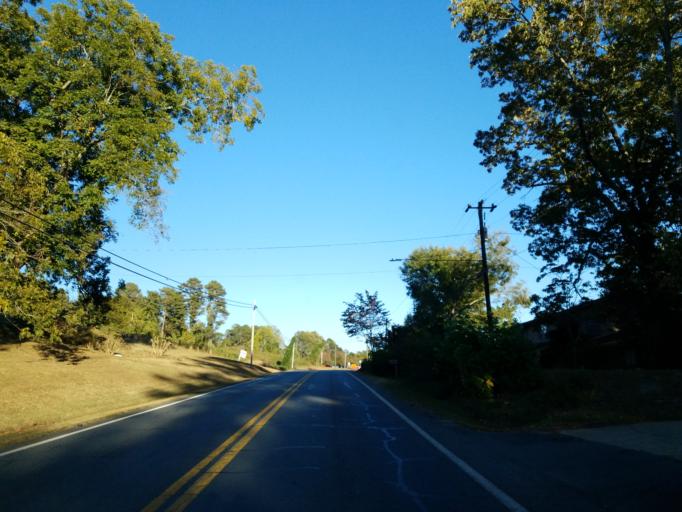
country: US
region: Georgia
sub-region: Dawson County
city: Dawsonville
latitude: 34.4217
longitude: -84.1269
